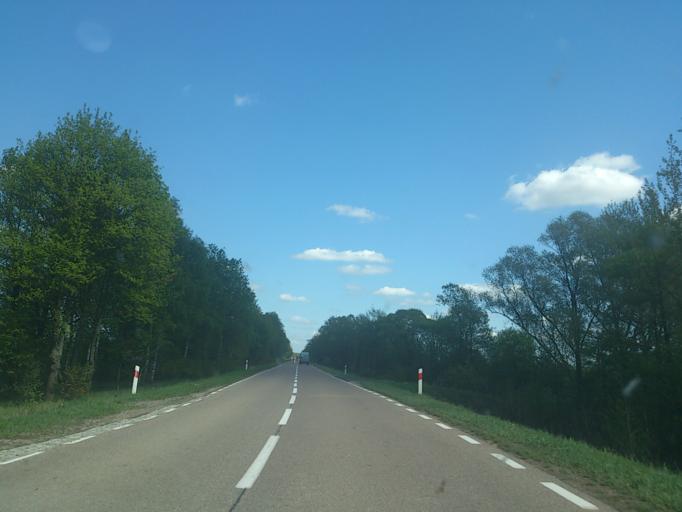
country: PL
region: Podlasie
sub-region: Powiat lomzynski
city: Wizna
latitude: 53.2027
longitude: 22.4608
